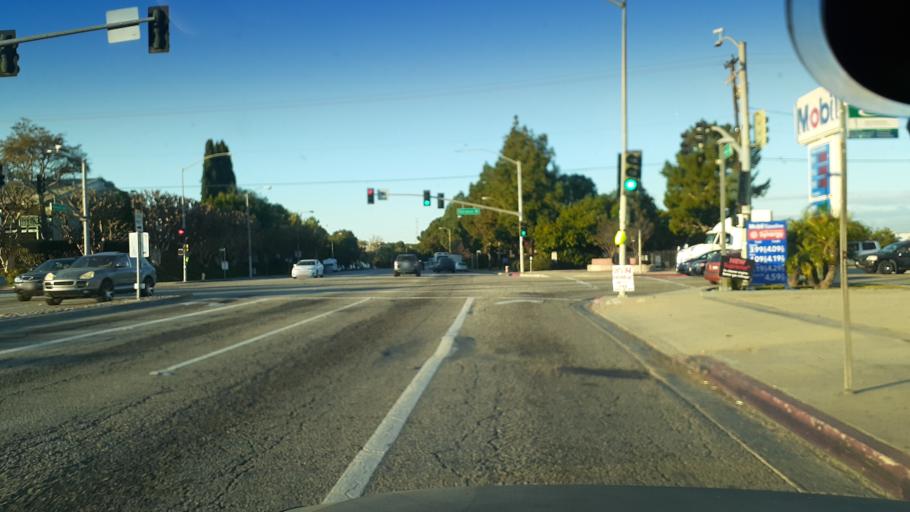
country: US
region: California
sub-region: Los Angeles County
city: Carson
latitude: 33.8417
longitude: -118.2899
